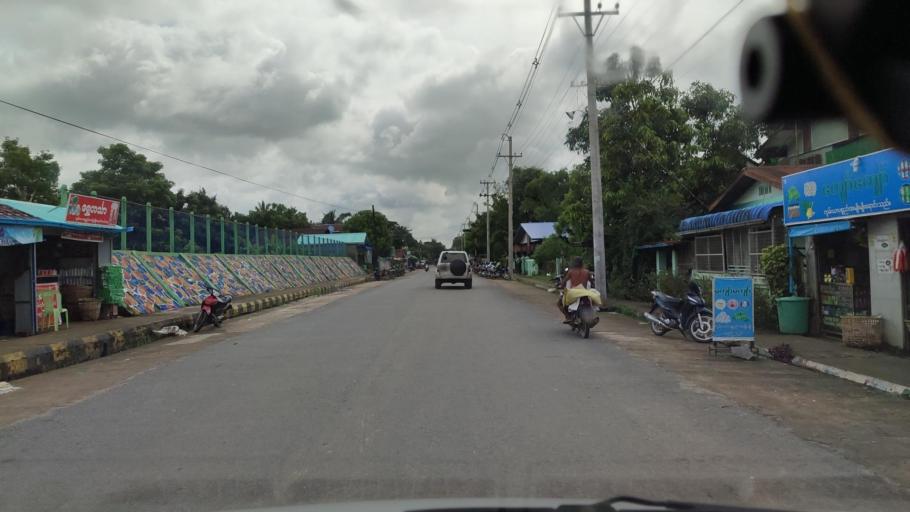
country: MM
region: Bago
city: Thanatpin
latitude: 17.0891
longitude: 96.4585
